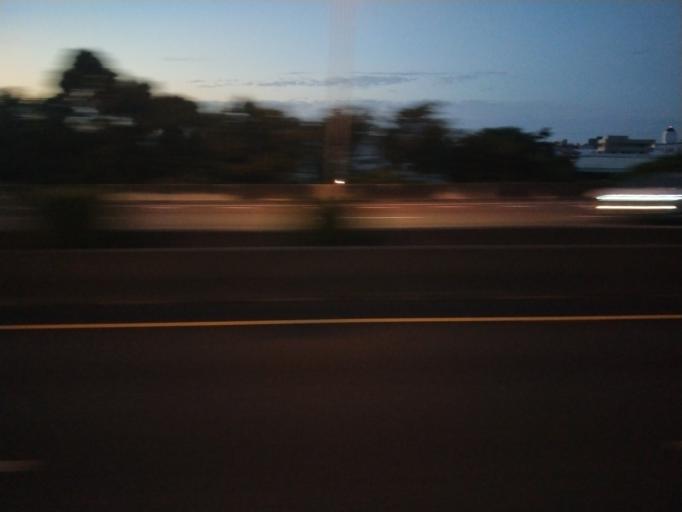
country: TW
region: Taiwan
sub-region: Taichung City
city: Taichung
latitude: 24.2024
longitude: 120.6508
